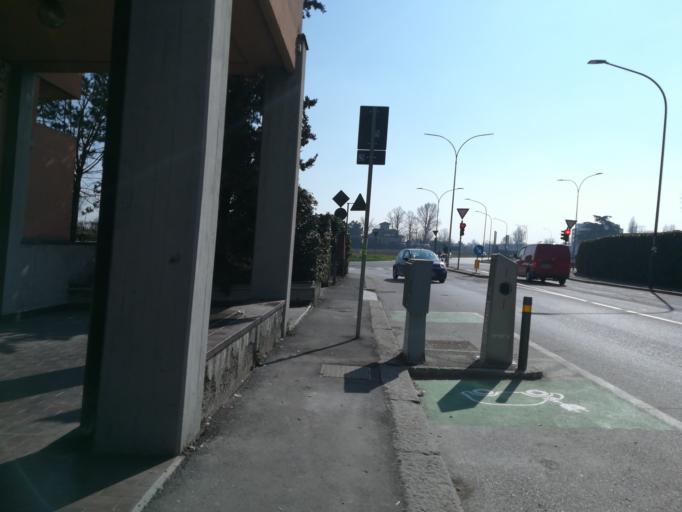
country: IT
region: Emilia-Romagna
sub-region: Provincia di Bologna
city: Progresso
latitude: 44.5400
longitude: 11.3582
